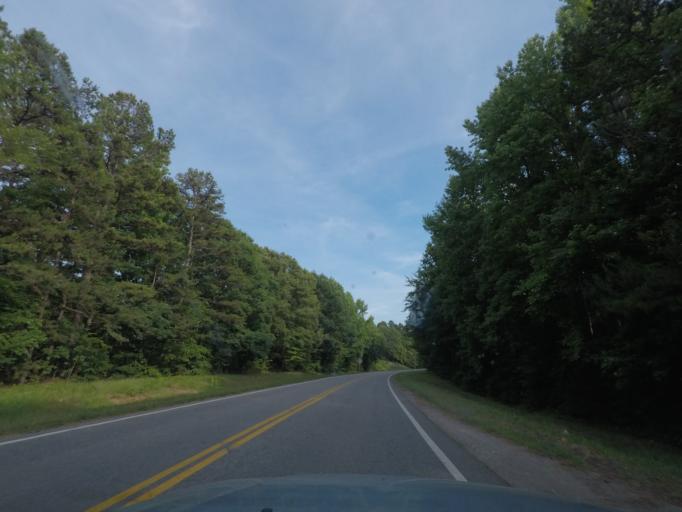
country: US
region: Virginia
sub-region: Mecklenburg County
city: Clarksville
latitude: 36.5981
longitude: -78.5501
